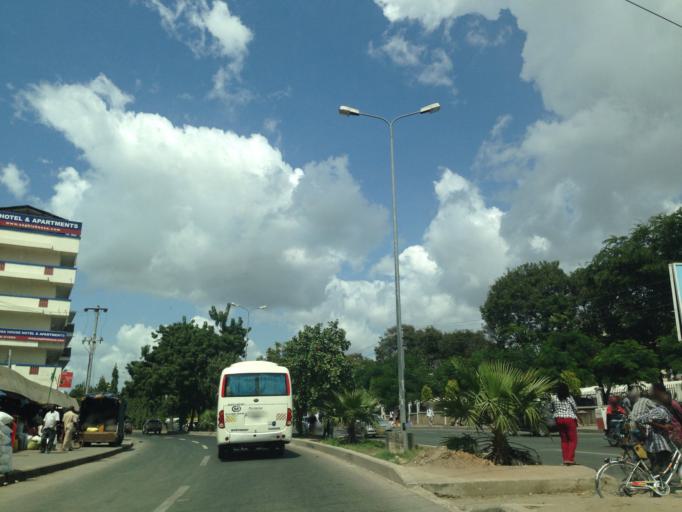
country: TZ
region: Dar es Salaam
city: Dar es Salaam
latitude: -6.8170
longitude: 39.2801
